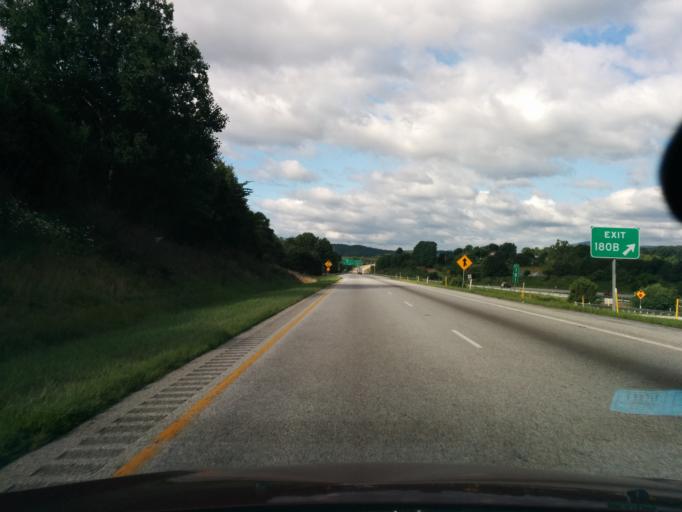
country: US
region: Virginia
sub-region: Rockbridge County
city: Glasgow
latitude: 37.6741
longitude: -79.5023
